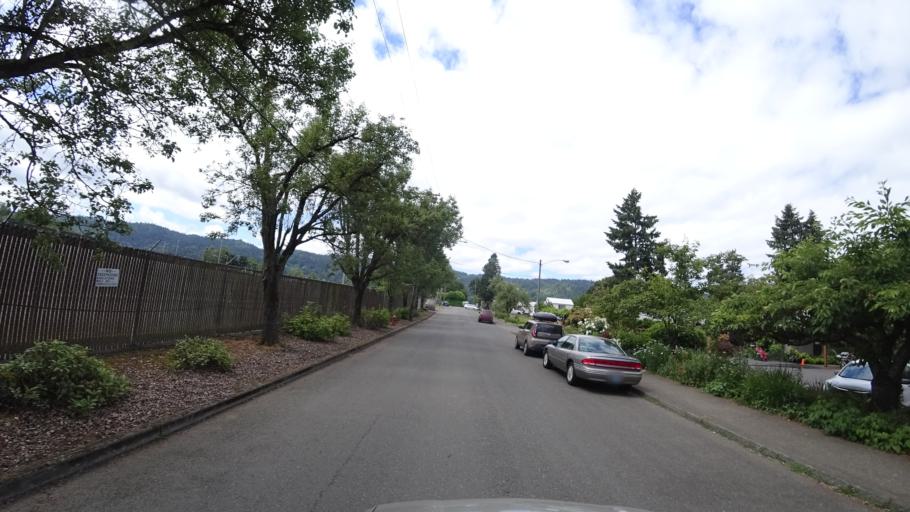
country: US
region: Oregon
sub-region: Washington County
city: West Haven
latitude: 45.6031
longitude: -122.7669
